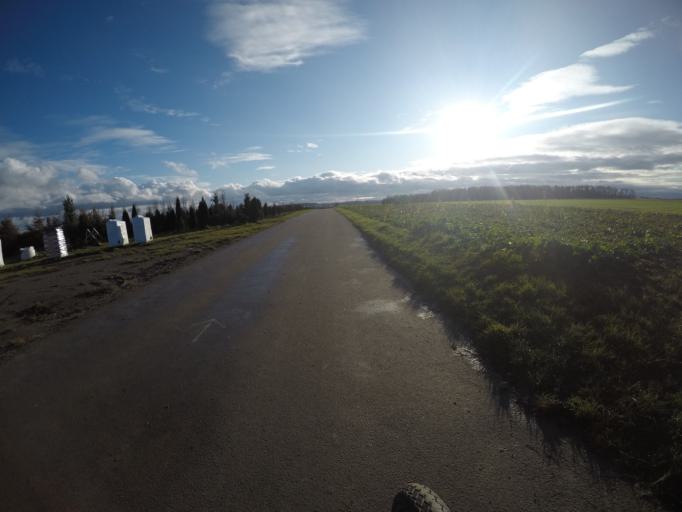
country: DE
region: Baden-Wuerttemberg
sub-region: Regierungsbezirk Stuttgart
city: Bondorf
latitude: 48.5475
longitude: 8.8745
